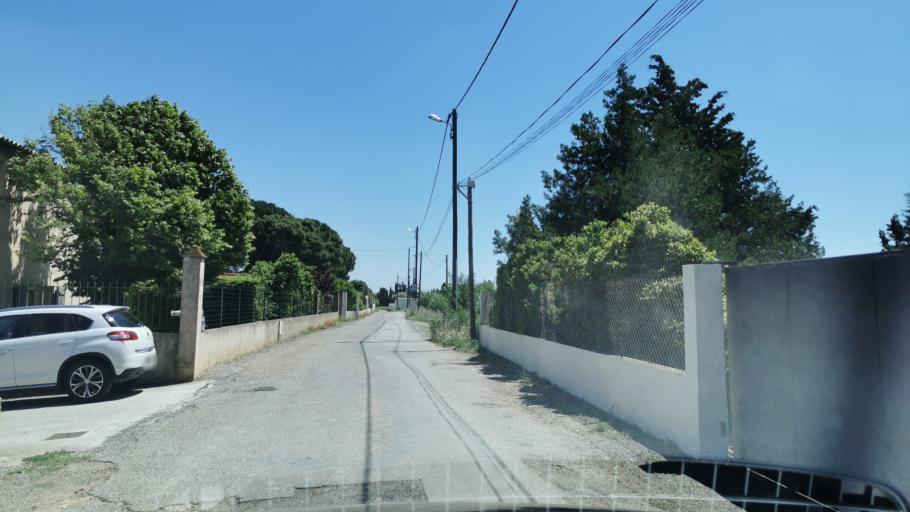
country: FR
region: Languedoc-Roussillon
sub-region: Departement de l'Aude
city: Saint-Marcel-sur-Aude
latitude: 43.2645
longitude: 2.9509
